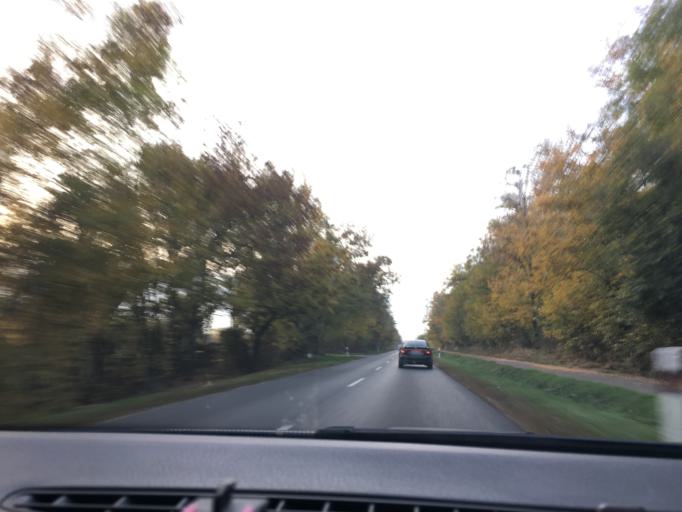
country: HU
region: Szabolcs-Szatmar-Bereg
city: Nagykallo
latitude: 47.8676
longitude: 21.8770
